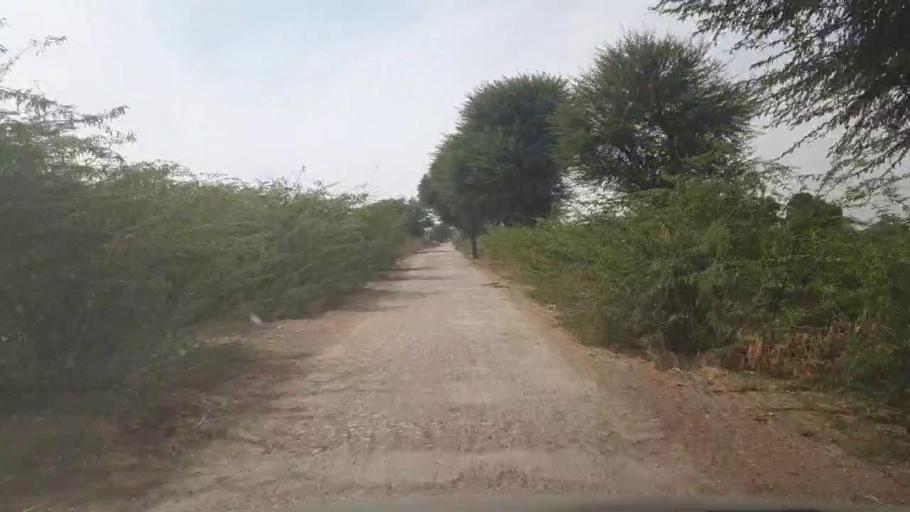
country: PK
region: Sindh
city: Kunri
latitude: 25.2382
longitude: 69.5947
